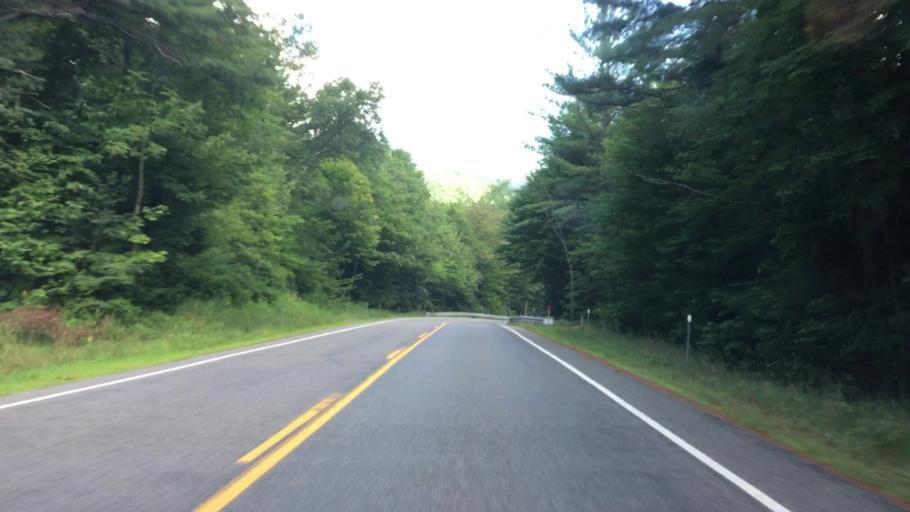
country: US
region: New Hampshire
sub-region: Grafton County
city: Woodstock
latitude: 44.0774
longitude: -71.7974
